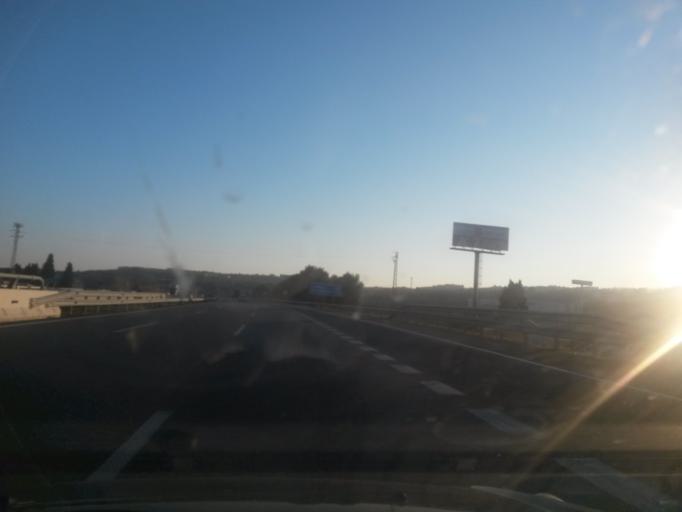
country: ES
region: Catalonia
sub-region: Provincia de Girona
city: Pont de Molins
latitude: 42.2974
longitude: 2.9417
